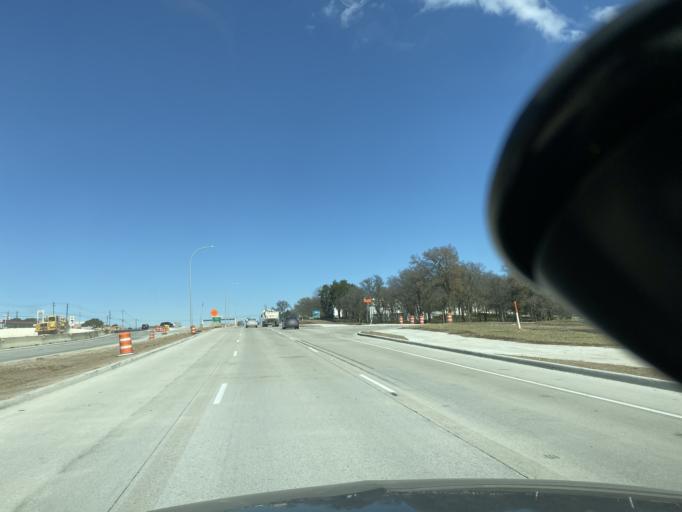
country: US
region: Texas
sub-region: Travis County
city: Austin
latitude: 30.2729
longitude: -97.6681
